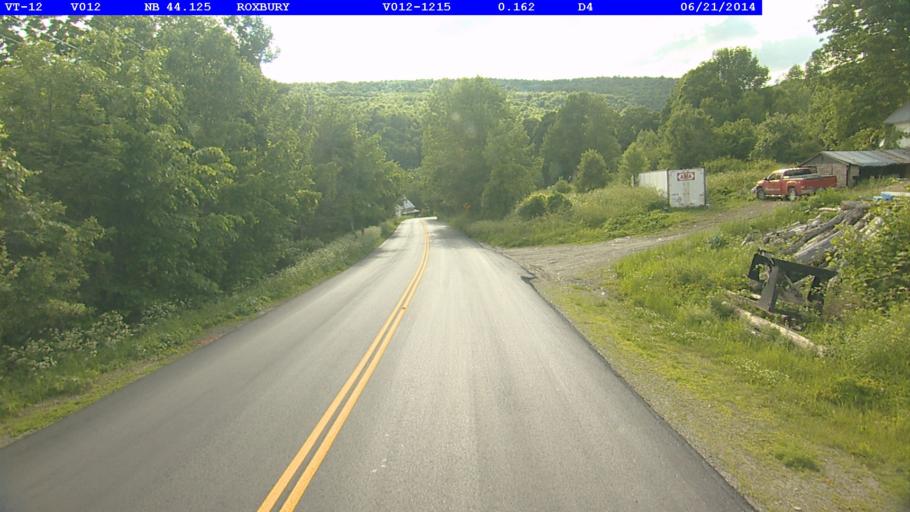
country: US
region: Vermont
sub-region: Washington County
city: Northfield
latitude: 44.0766
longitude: -72.6460
